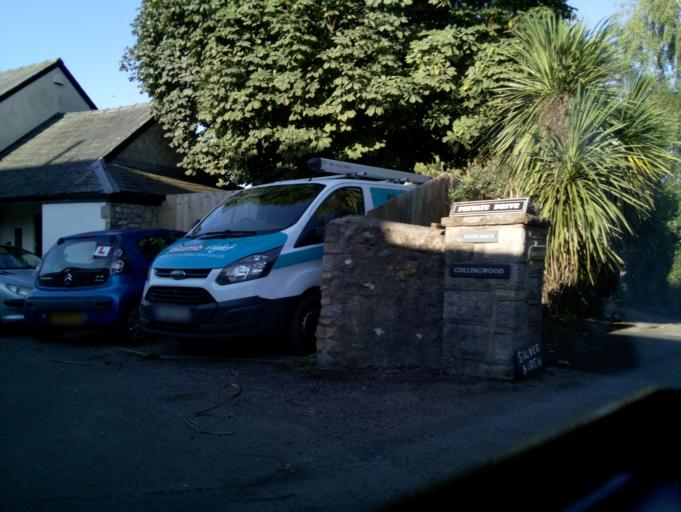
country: GB
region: Wales
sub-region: Monmouthshire
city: Chepstow
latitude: 51.6288
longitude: -2.6961
